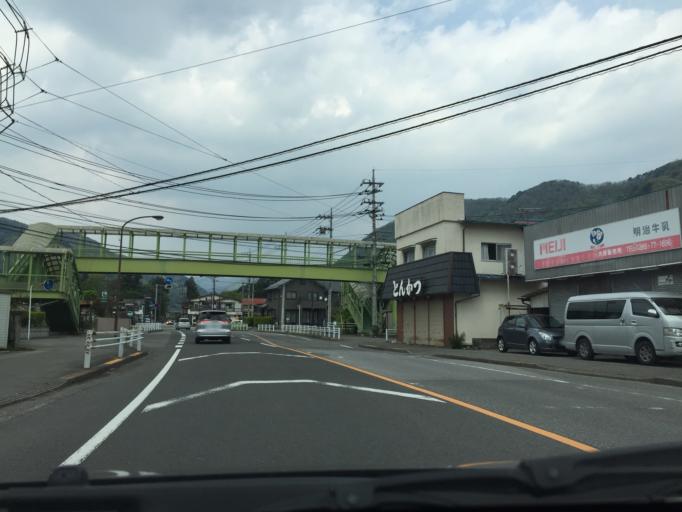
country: JP
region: Tochigi
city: Imaichi
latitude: 36.8175
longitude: 139.7158
